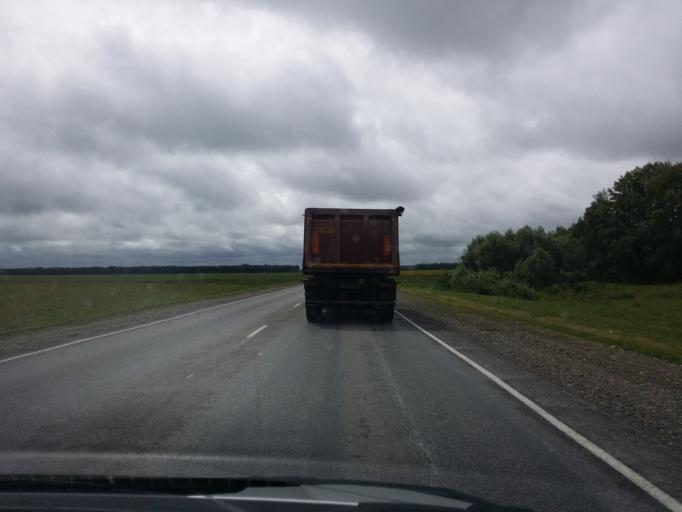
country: RU
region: Altai Krai
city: Zonal'noye
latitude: 52.8561
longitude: 84.8550
